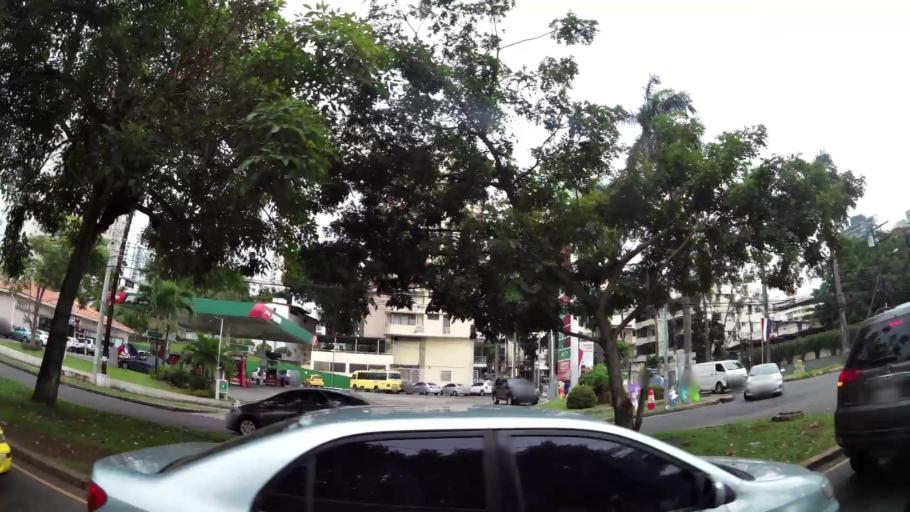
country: PA
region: Panama
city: Panama
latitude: 8.9869
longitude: -79.5320
